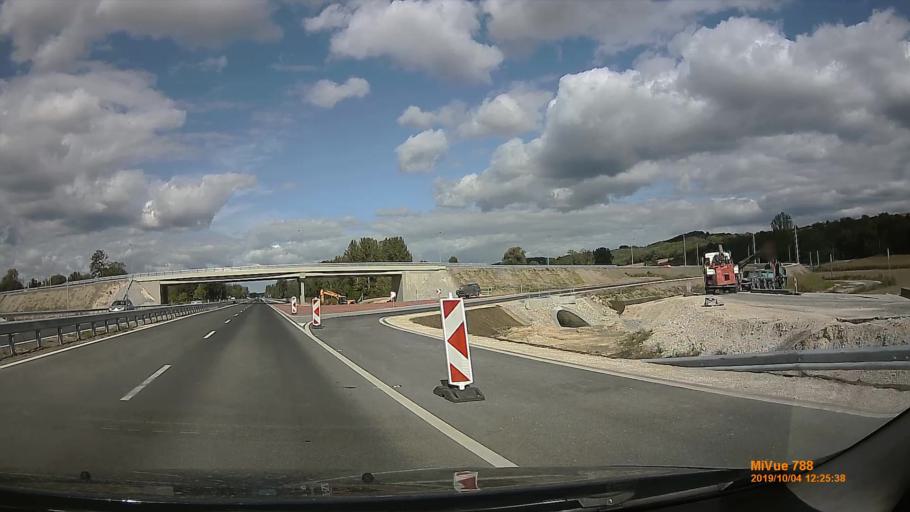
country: HU
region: Somogy
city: Karad
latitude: 46.6660
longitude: 17.7830
